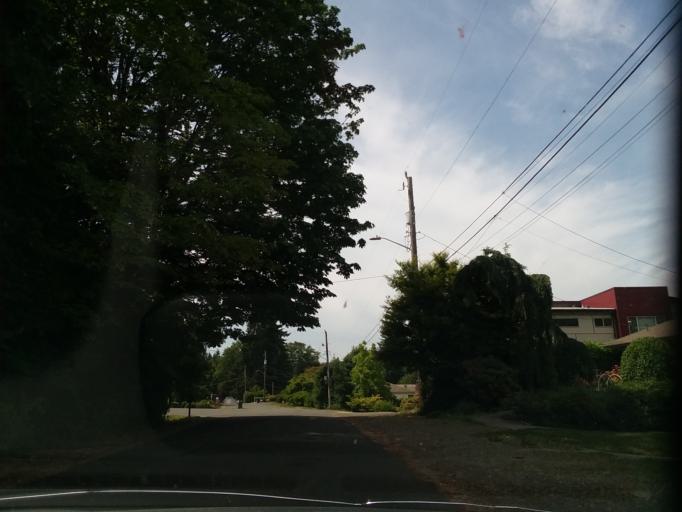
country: US
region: Washington
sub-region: King County
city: Lake Forest Park
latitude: 47.7226
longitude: -122.3103
